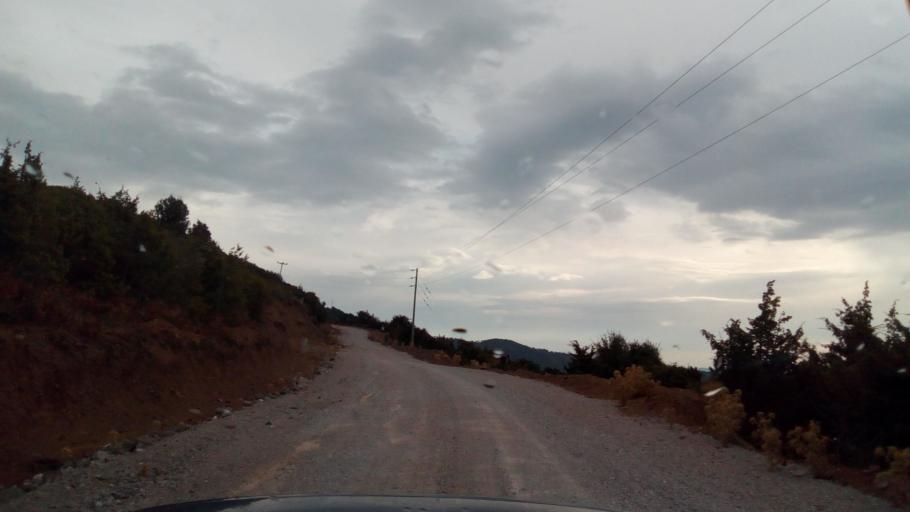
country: GR
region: West Greece
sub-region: Nomos Achaias
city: Kamarai
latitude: 38.4386
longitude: 22.0602
